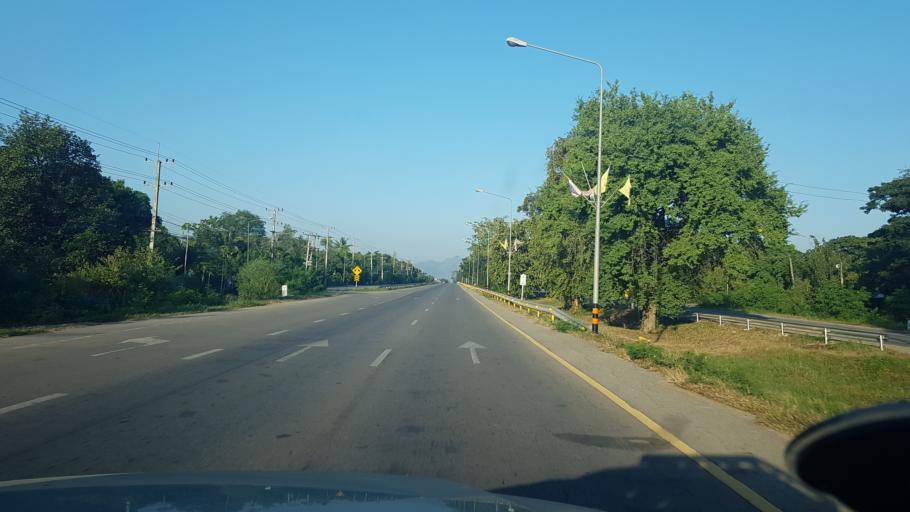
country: TH
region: Chaiyaphum
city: Khon San
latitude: 16.5902
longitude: 101.9879
